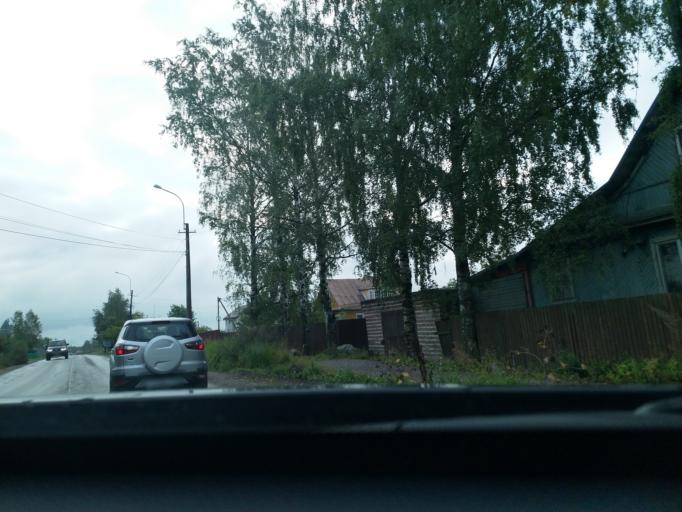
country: RU
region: Leningrad
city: Nikol'skoye
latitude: 59.6919
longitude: 30.7853
